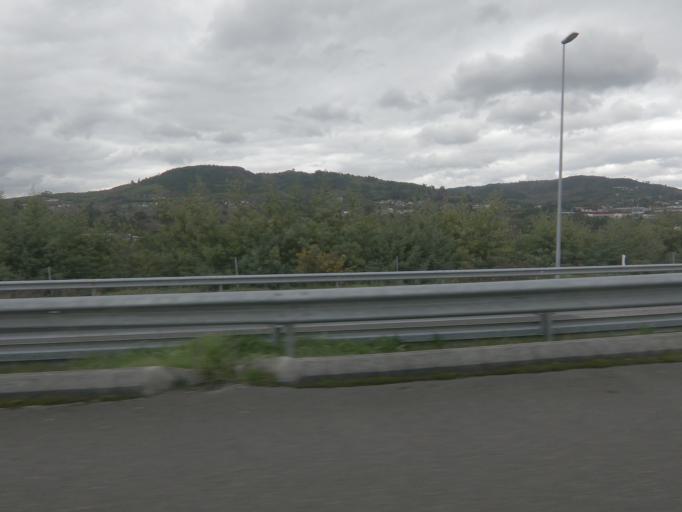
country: ES
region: Galicia
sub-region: Provincia de Ourense
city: Punxin
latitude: 42.3417
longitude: -7.9953
